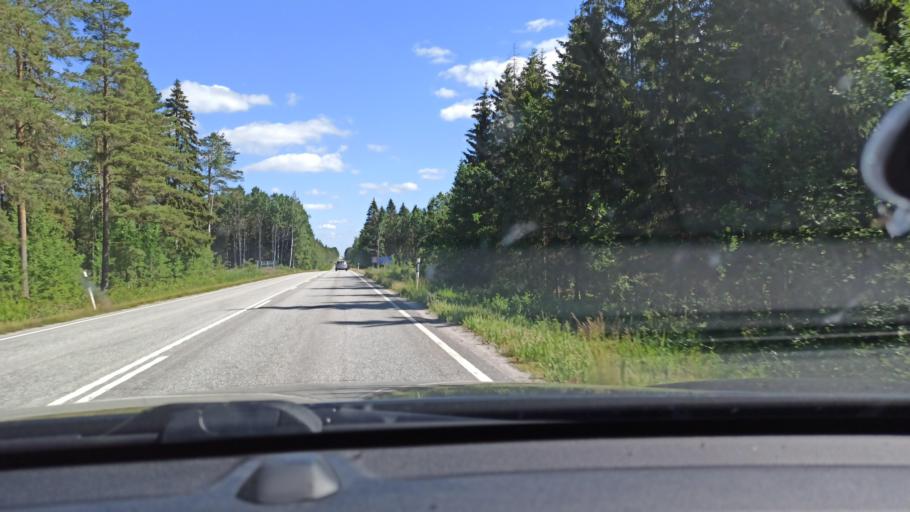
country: FI
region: Ostrobothnia
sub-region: Vaasa
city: Malax
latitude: 62.9736
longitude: 21.5994
